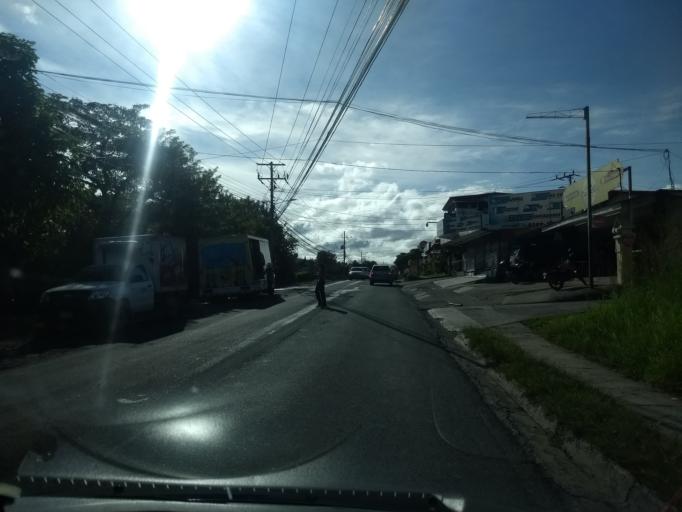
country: CR
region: San Jose
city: Santa Ana
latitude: 9.9466
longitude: -84.1614
